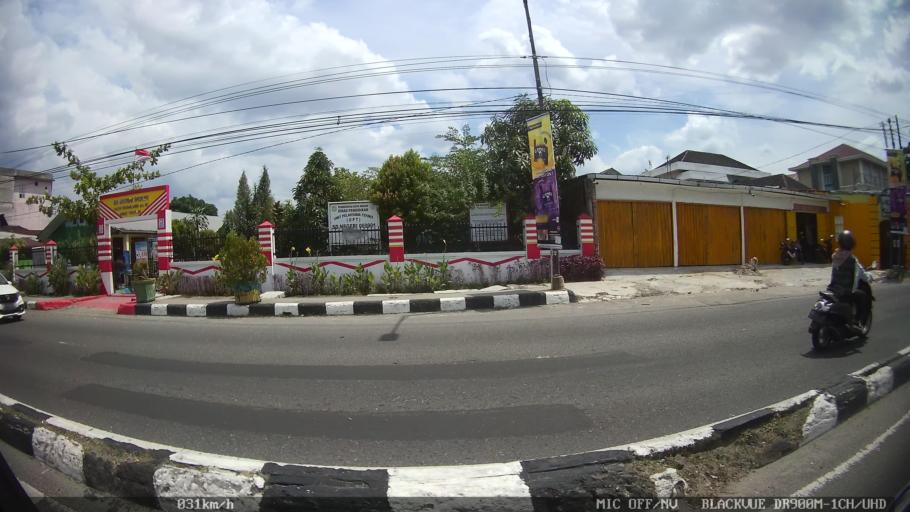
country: ID
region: North Sumatra
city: Medan
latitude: 3.5712
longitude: 98.6637
